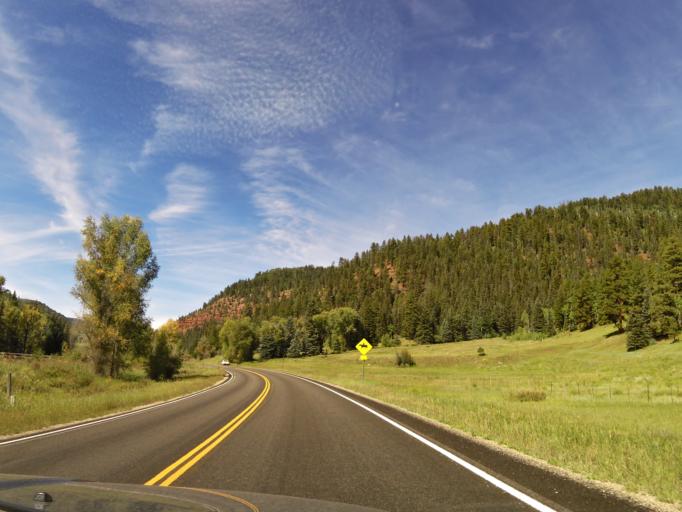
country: US
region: Colorado
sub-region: Montezuma County
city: Mancos
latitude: 37.5937
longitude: -108.1334
